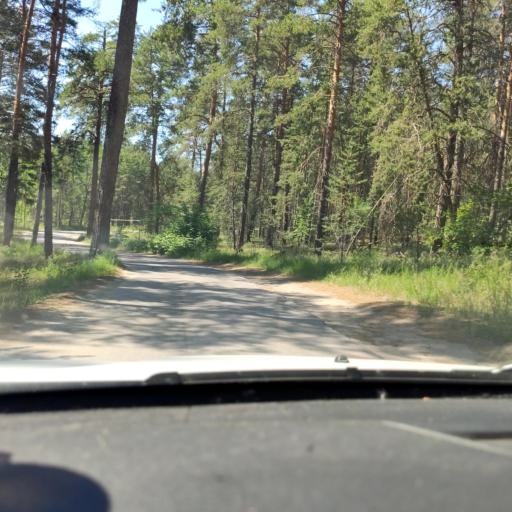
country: RU
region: Samara
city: Pribrezhnyy
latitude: 53.4776
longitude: 49.8050
